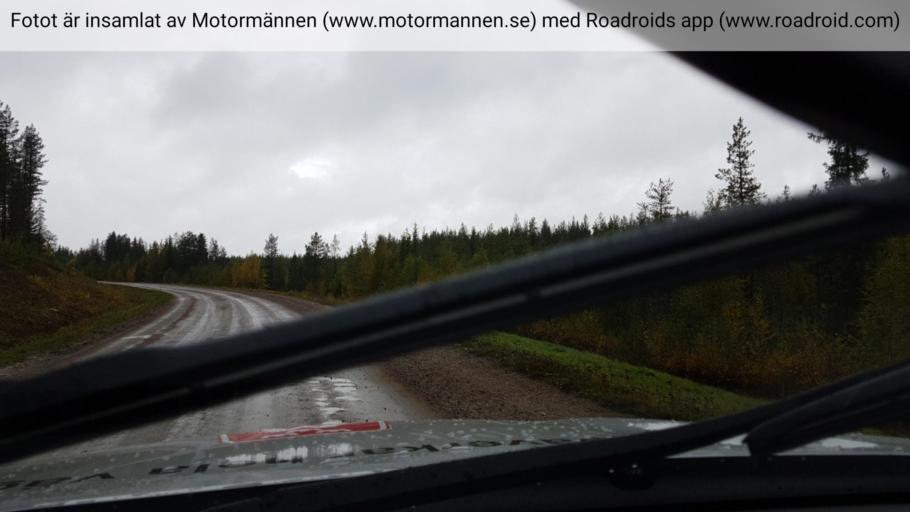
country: SE
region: Norrbotten
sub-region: Alvsbyns Kommun
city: AElvsbyn
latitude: 66.2646
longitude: 21.0700
